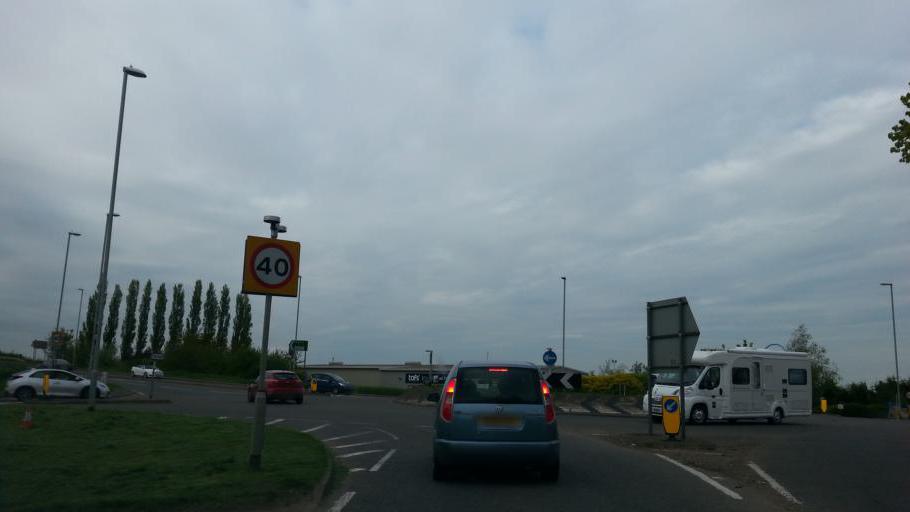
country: GB
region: England
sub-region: Cambridgeshire
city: March
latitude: 52.5582
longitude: 0.0673
